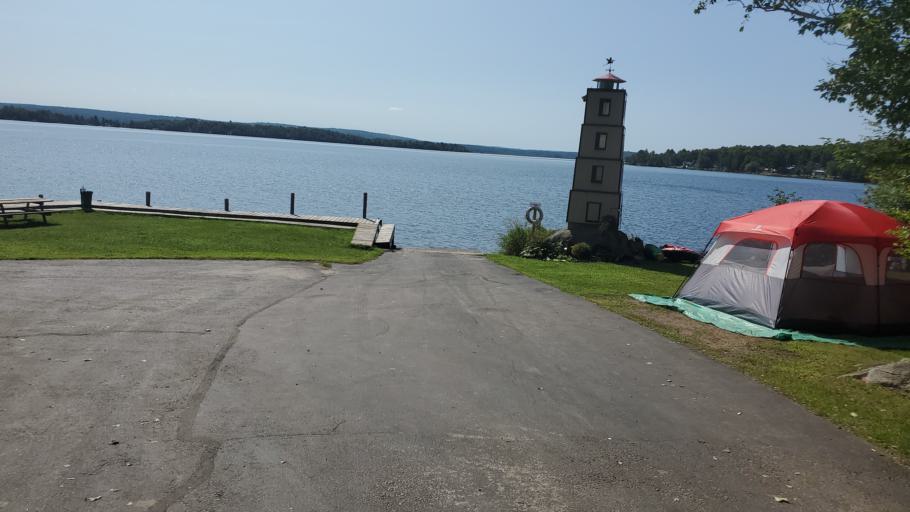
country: CA
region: Ontario
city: Powassan
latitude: 46.2256
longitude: -79.2286
